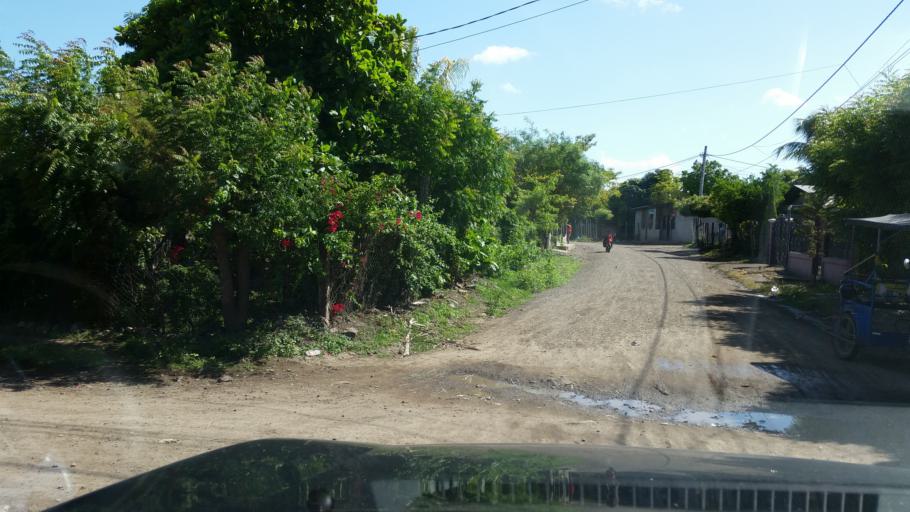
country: NI
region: Matagalpa
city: Ciudad Dario
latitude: 12.8612
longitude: -86.0928
